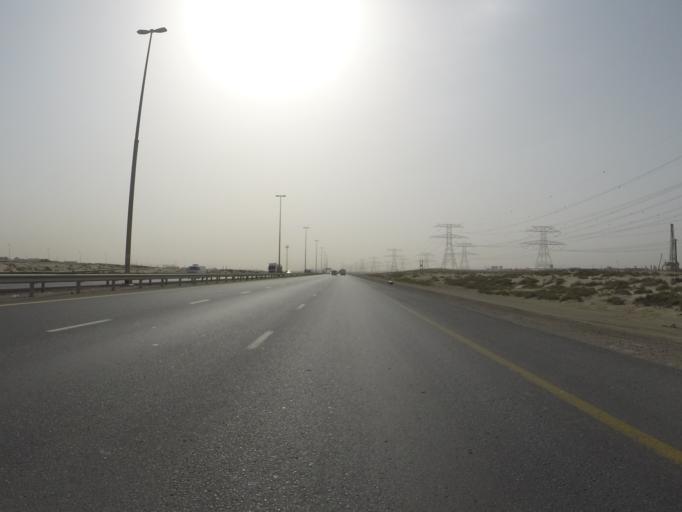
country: AE
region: Dubai
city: Dubai
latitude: 25.0171
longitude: 55.1216
